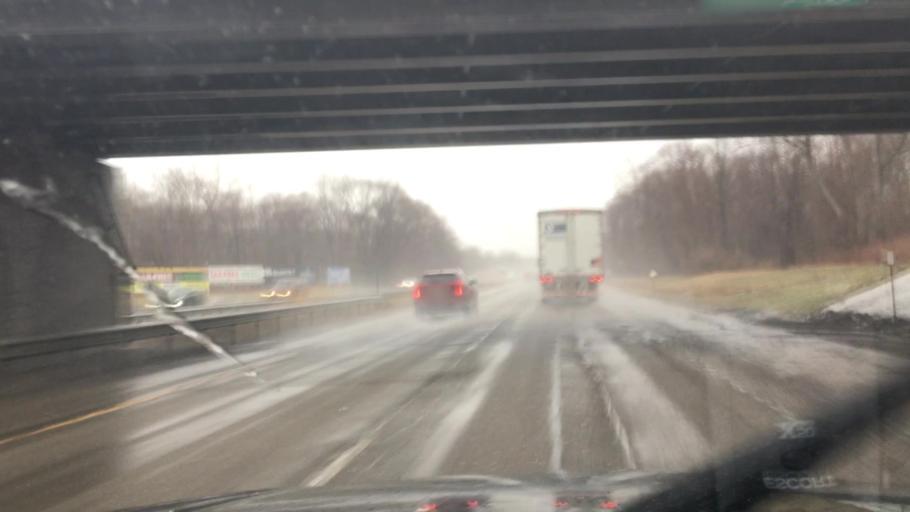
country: US
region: New York
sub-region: Erie County
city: Lake Erie Beach
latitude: 42.5647
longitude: -79.0920
